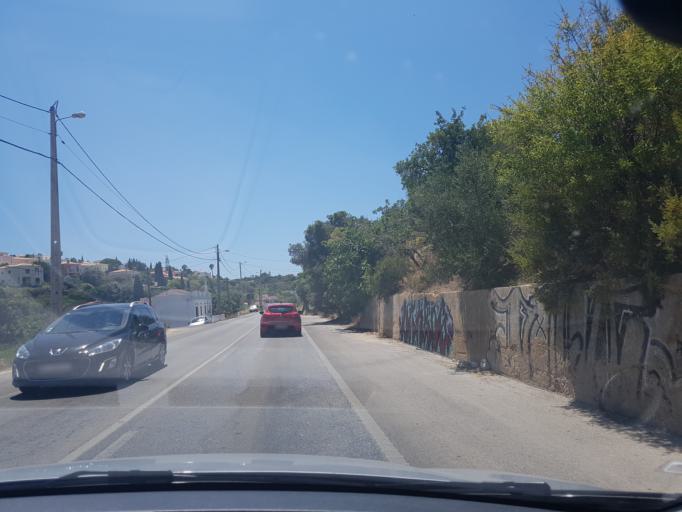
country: PT
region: Faro
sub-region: Lagoa
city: Carvoeiro
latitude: 37.1043
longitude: -8.4636
